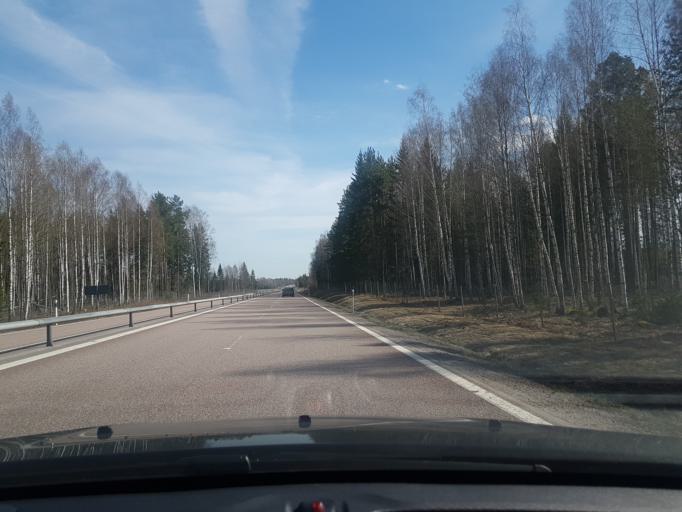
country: SE
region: Dalarna
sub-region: Avesta Kommun
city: Avesta
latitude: 60.1434
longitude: 16.2361
